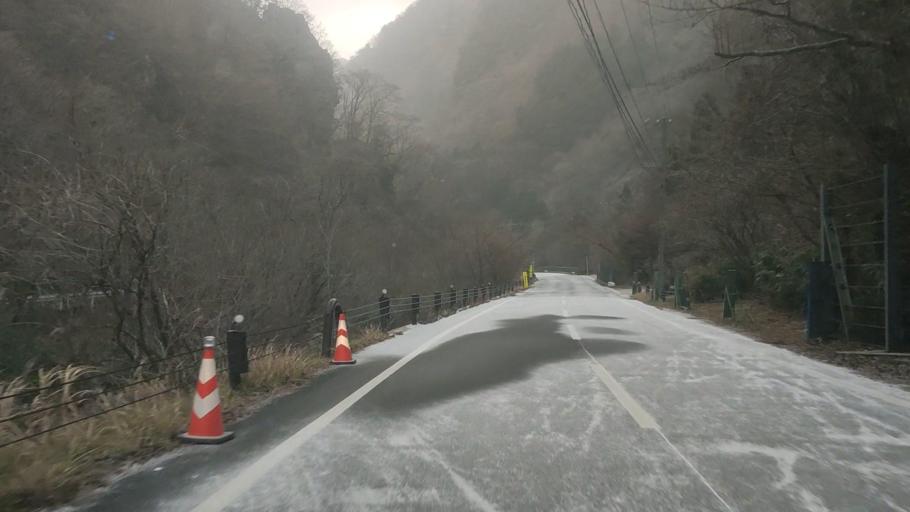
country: JP
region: Kumamoto
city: Matsubase
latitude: 32.5565
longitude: 130.9215
